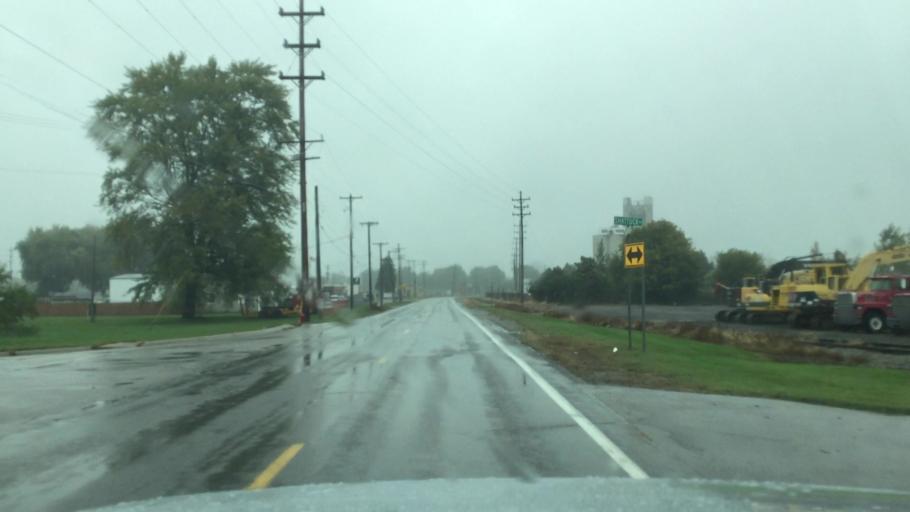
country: US
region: Michigan
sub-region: Saginaw County
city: Carrollton
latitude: 43.4505
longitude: -83.9375
